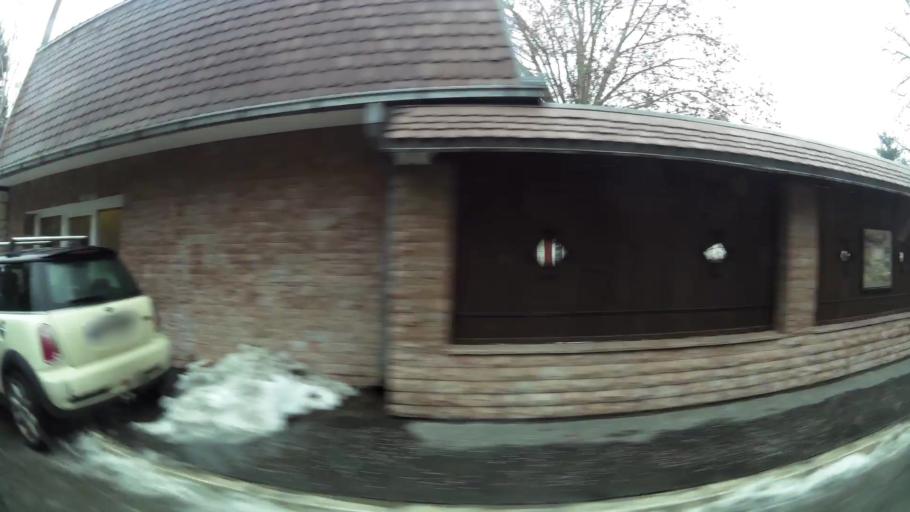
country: RS
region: Central Serbia
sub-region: Belgrade
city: Savski Venac
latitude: 44.7846
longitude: 20.4452
